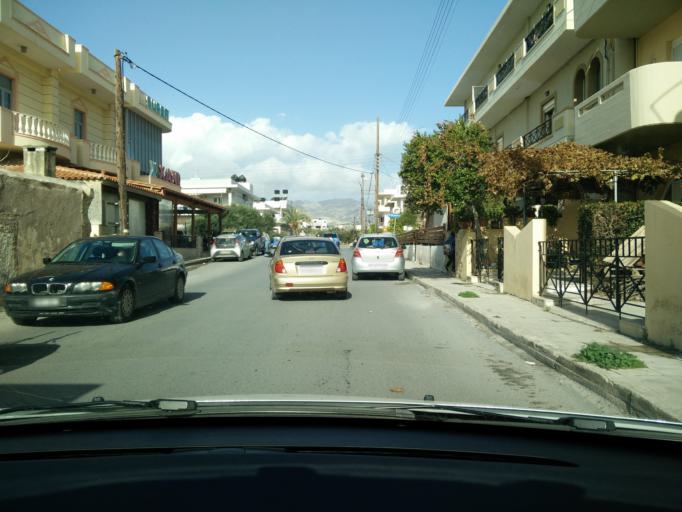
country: GR
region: Crete
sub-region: Nomos Lasithiou
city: Ierapetra
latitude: 35.0137
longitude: 25.7365
